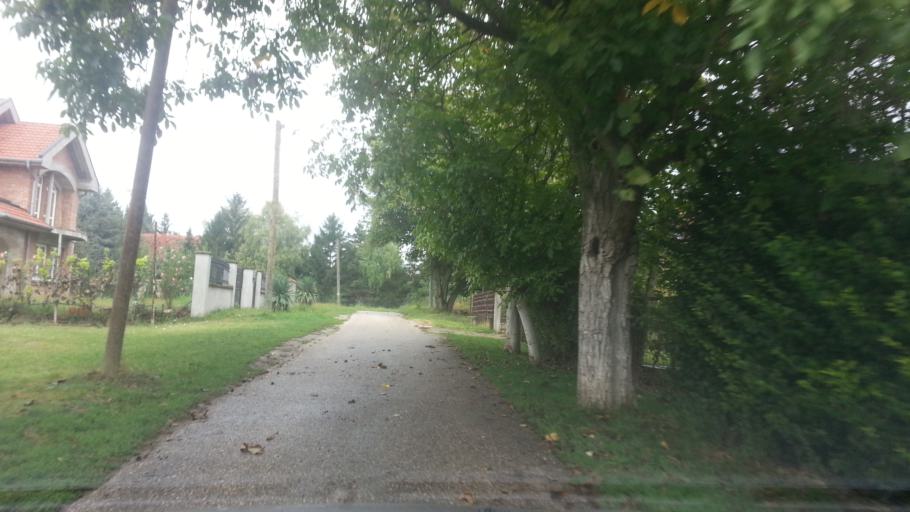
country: RS
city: Novi Banovci
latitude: 44.9416
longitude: 20.2952
